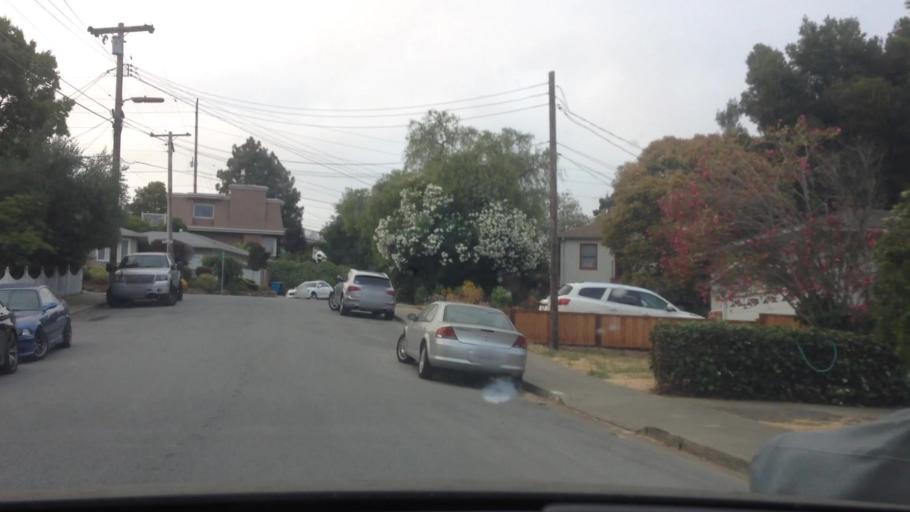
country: US
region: California
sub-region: San Mateo County
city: Emerald Lake Hills
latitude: 37.4661
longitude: -122.2475
